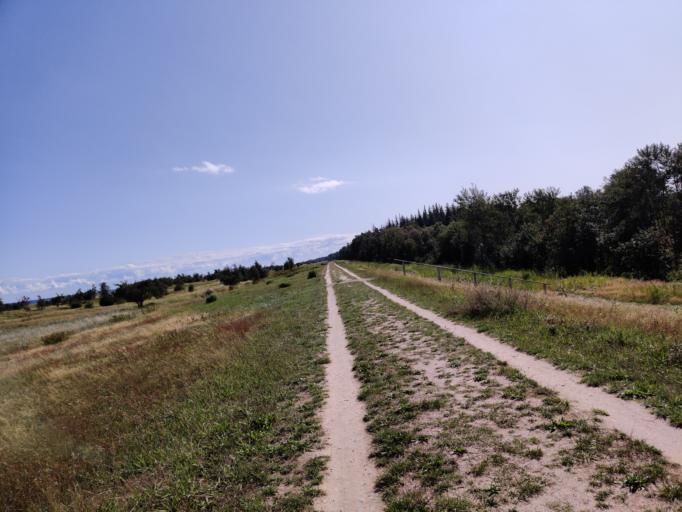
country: DK
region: Zealand
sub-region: Guldborgsund Kommune
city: Nykobing Falster
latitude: 54.6378
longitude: 11.9610
